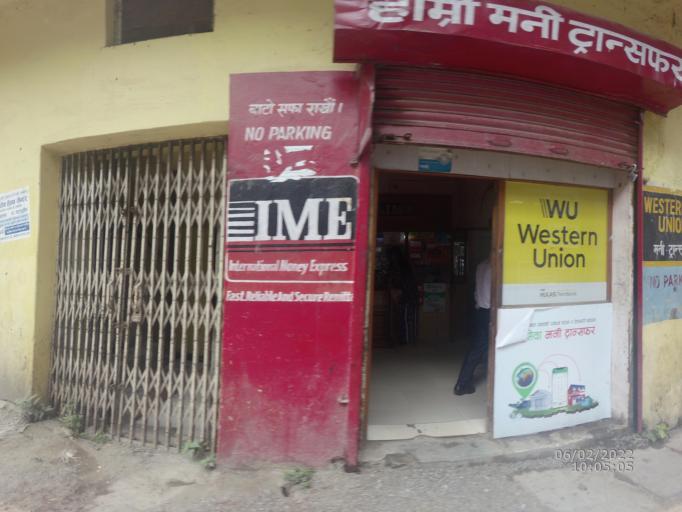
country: NP
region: Western Region
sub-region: Lumbini Zone
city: Bhairahawa
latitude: 27.5076
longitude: 83.4515
